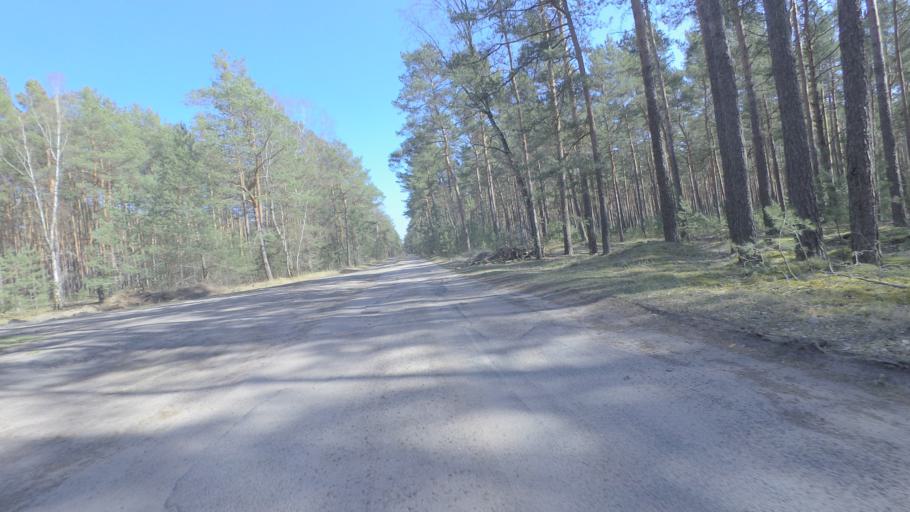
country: DE
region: Brandenburg
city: Halbe
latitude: 52.1741
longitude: 13.7405
